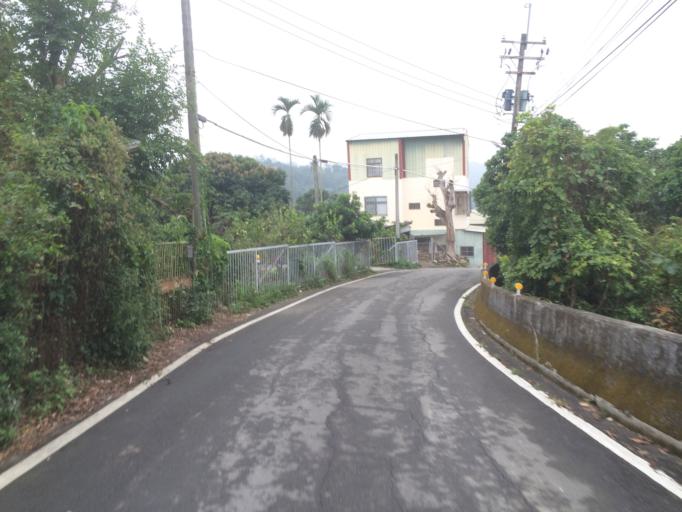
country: TW
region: Taiwan
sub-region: Taichung City
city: Taichung
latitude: 24.1607
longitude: 120.7718
